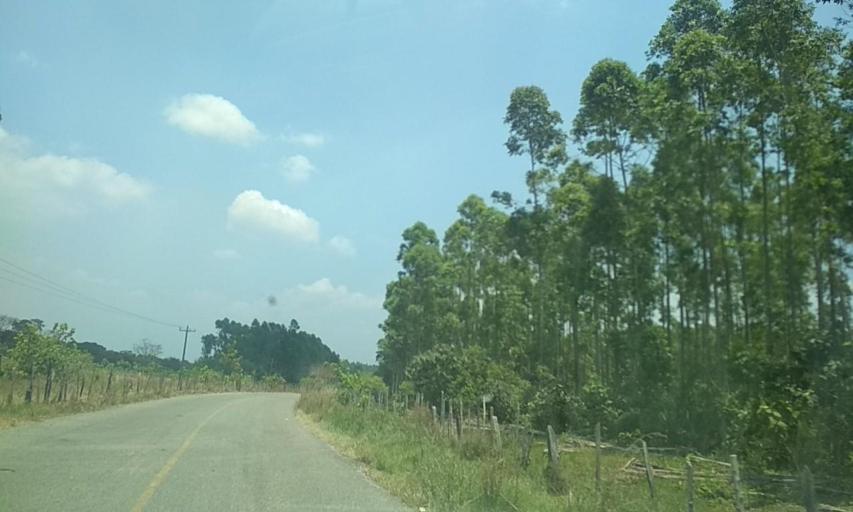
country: MX
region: Tabasco
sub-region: Huimanguillo
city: Francisco Rueda
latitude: 17.8422
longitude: -93.8965
